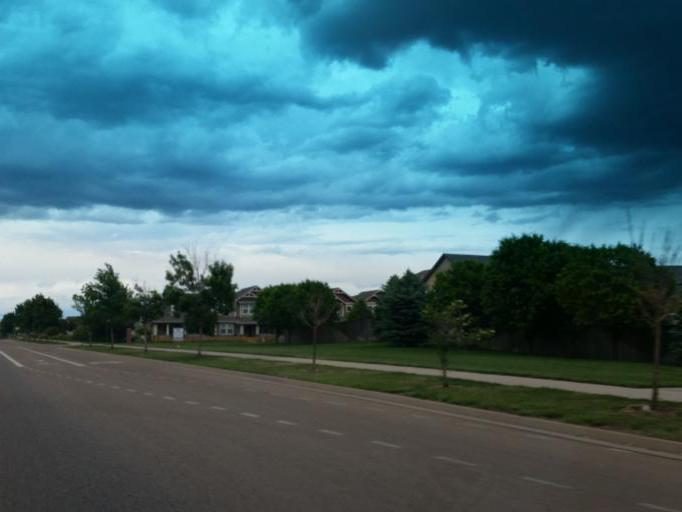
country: US
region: Colorado
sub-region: Larimer County
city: Fort Collins
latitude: 40.5554
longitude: -105.0391
